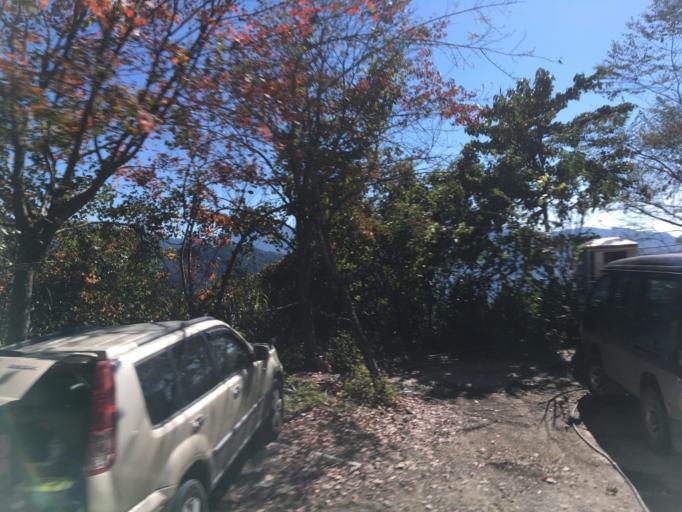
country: TW
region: Taiwan
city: Lugu
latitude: 23.4909
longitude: 120.7741
